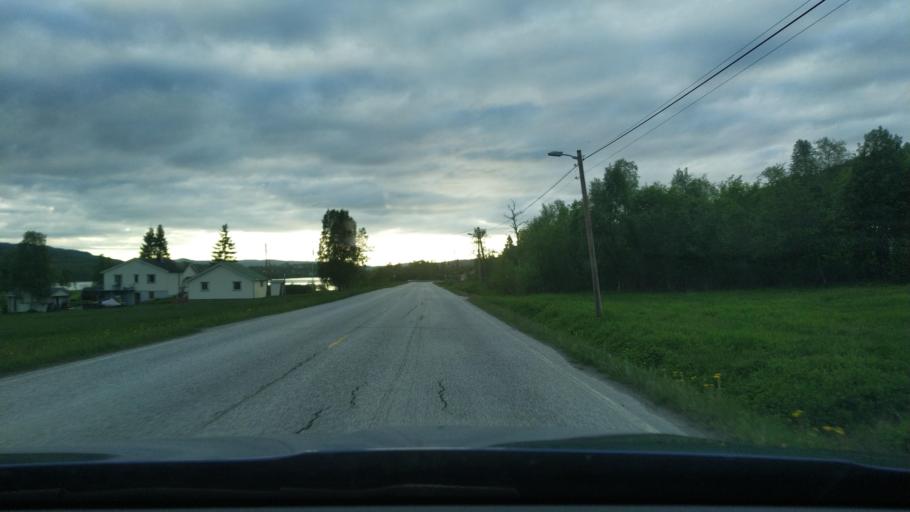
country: NO
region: Troms
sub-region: Sorreisa
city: Sorreisa
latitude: 69.1279
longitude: 18.2095
